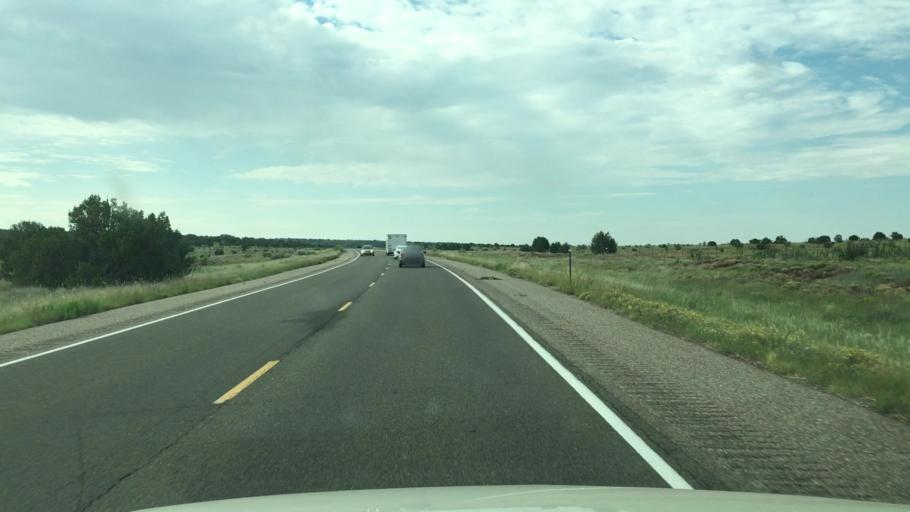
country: US
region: New Mexico
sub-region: Santa Fe County
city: Eldorado at Santa Fe
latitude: 35.2944
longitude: -105.8258
